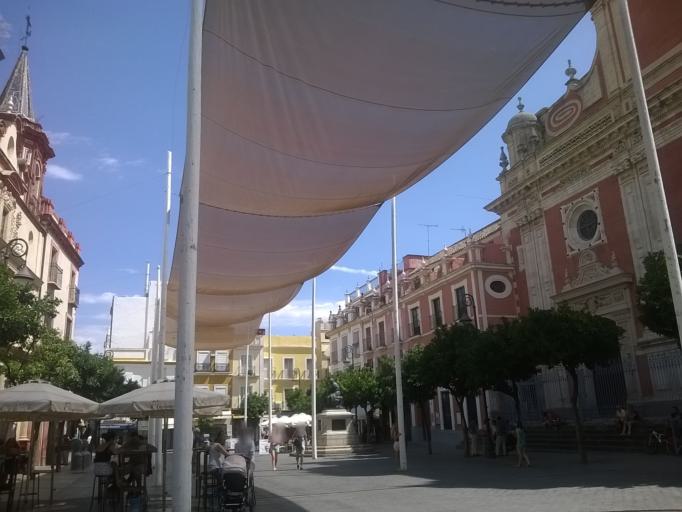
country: ES
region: Andalusia
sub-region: Provincia de Sevilla
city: Sevilla
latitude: 37.3897
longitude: -5.9932
